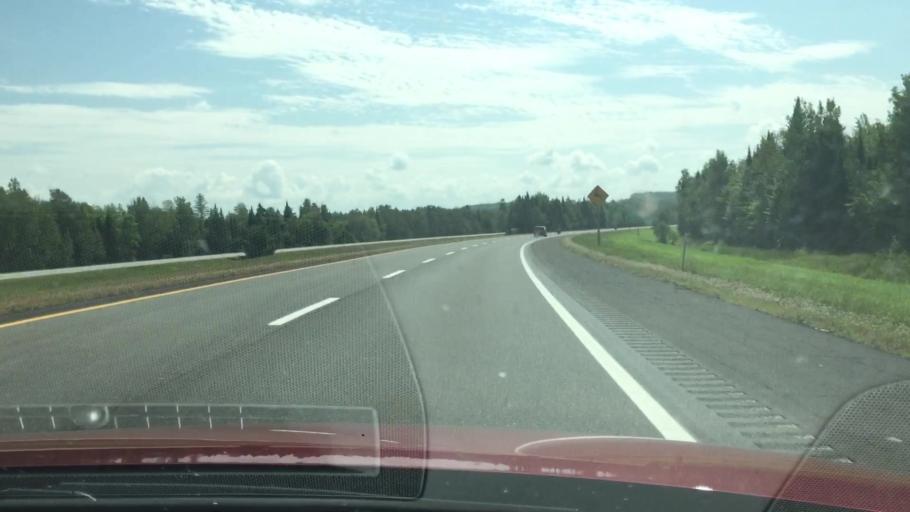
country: US
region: Maine
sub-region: Penobscot County
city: Patten
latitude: 45.9977
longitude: -68.2799
